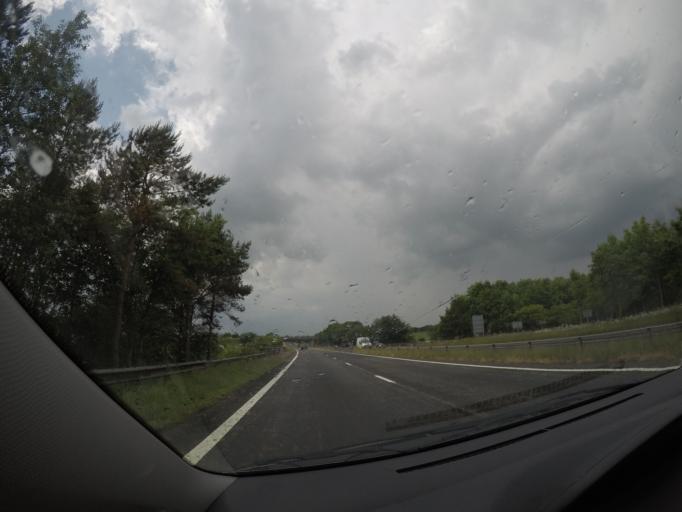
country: GB
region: England
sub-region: Cumbria
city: Appleby-in-Westmorland
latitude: 54.5869
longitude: -2.4953
